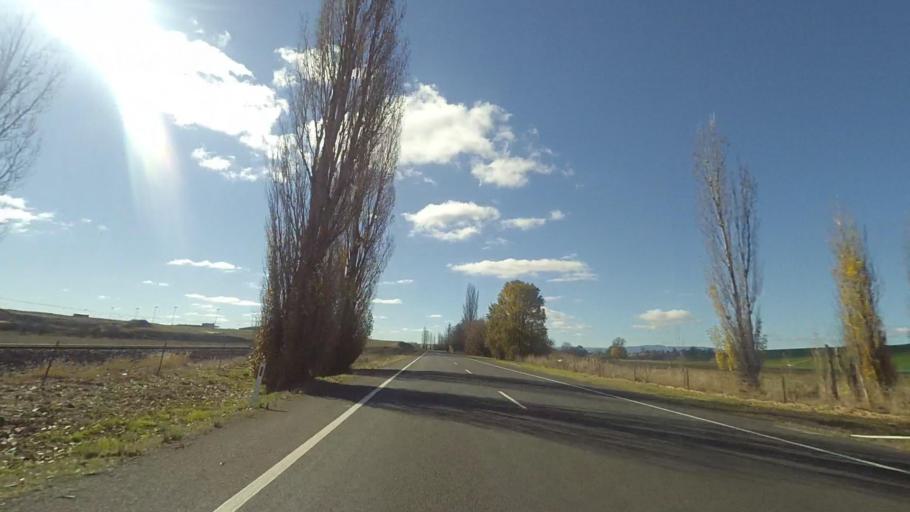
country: AU
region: New South Wales
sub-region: Bathurst Regional
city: Bathurst
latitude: -33.4567
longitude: 149.5749
